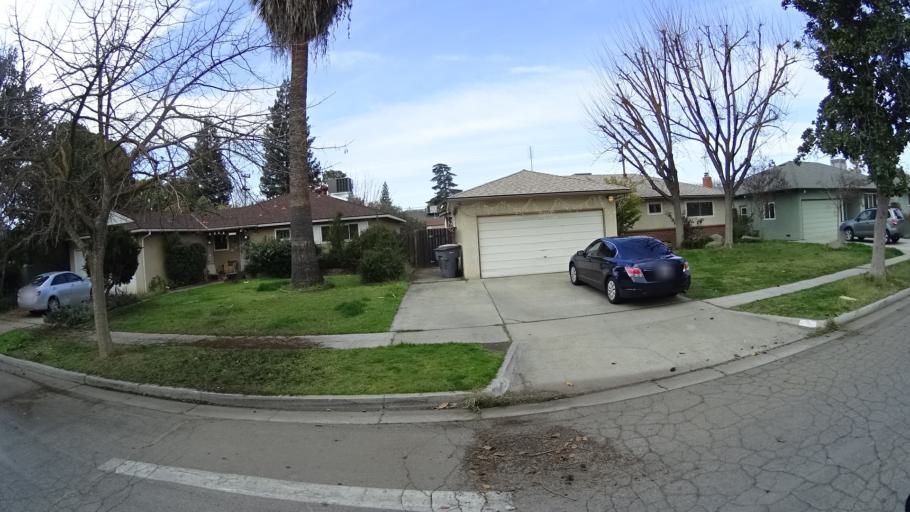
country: US
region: California
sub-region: Fresno County
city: Fresno
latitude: 36.8145
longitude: -119.7750
